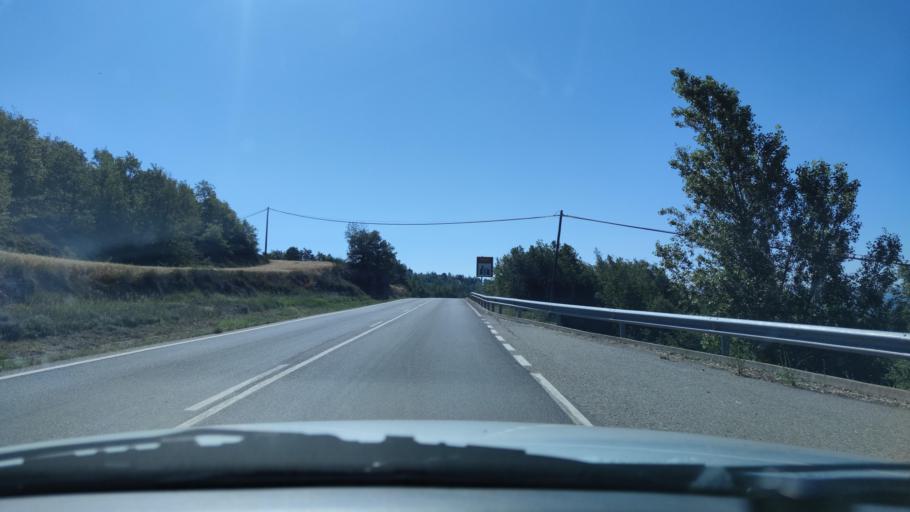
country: ES
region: Catalonia
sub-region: Provincia de Lleida
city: Solsona
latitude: 41.9125
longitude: 1.5156
